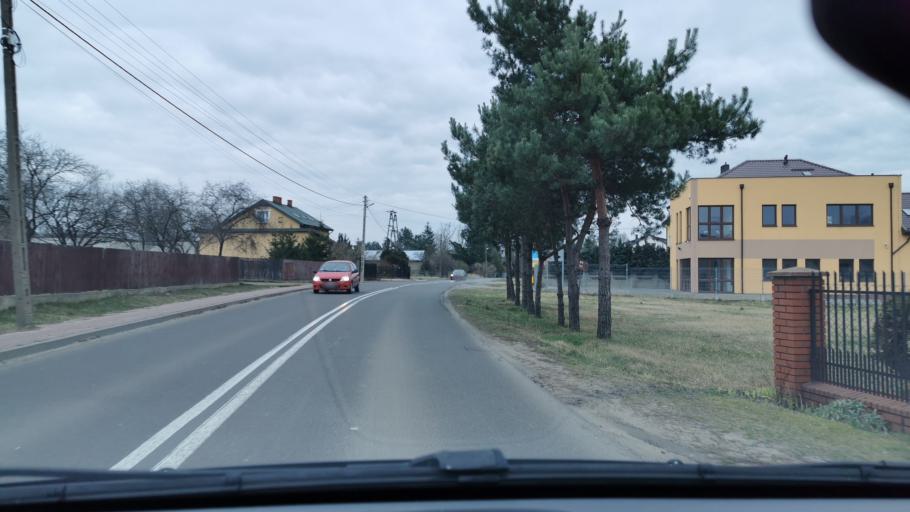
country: PL
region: Masovian Voivodeship
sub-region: Powiat zyrardowski
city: Radziejowice
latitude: 52.0086
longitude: 20.5457
